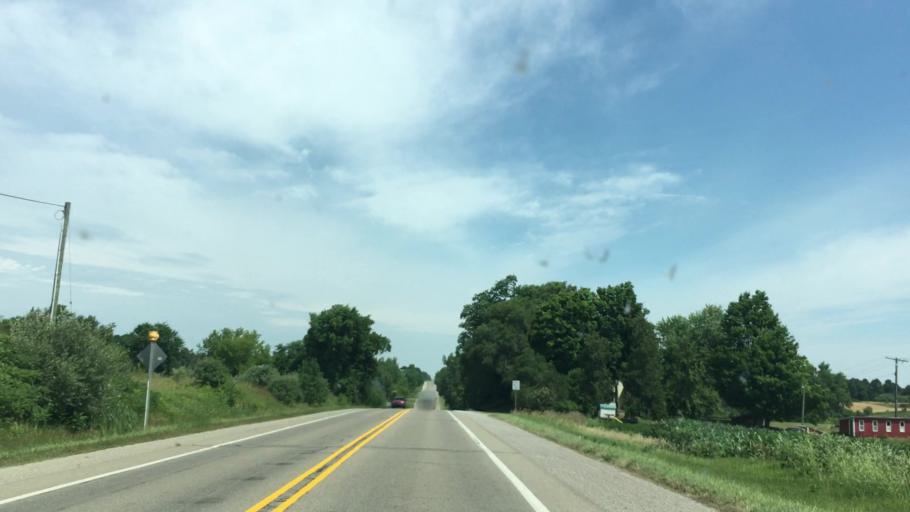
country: US
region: Michigan
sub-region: Lapeer County
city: Imlay City
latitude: 43.1063
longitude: -83.0721
